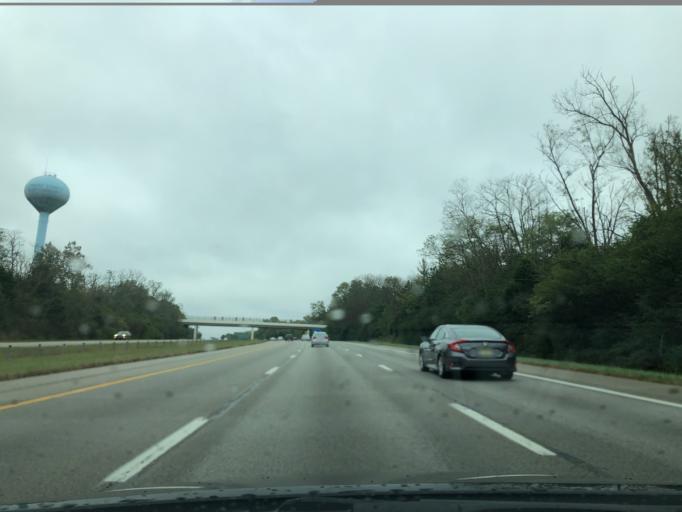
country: US
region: Ohio
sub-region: Hamilton County
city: The Village of Indian Hill
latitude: 39.2355
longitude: -84.2944
